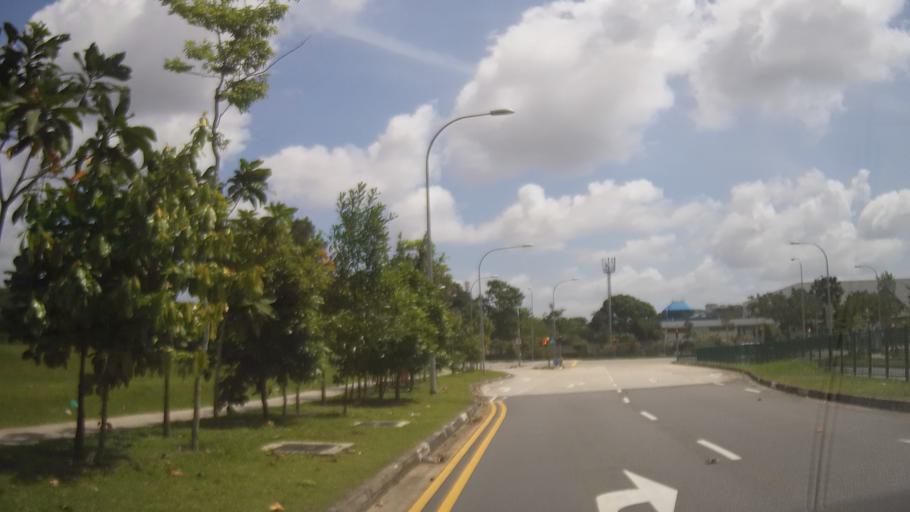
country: MY
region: Johor
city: Johor Bahru
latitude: 1.4289
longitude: 103.7552
